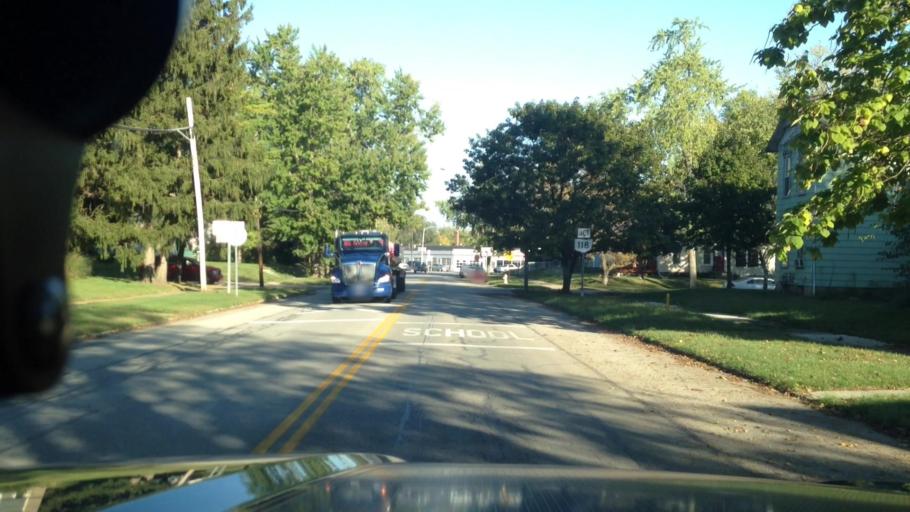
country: US
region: Ohio
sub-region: Darke County
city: Greenville
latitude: 40.1058
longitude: -84.6390
